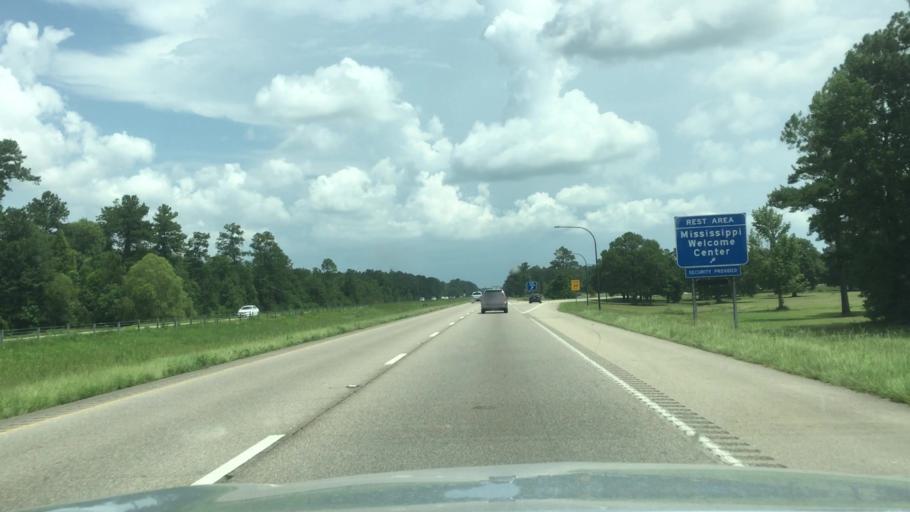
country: US
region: Mississippi
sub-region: Pearl River County
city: Nicholson
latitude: 30.4927
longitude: -89.6717
